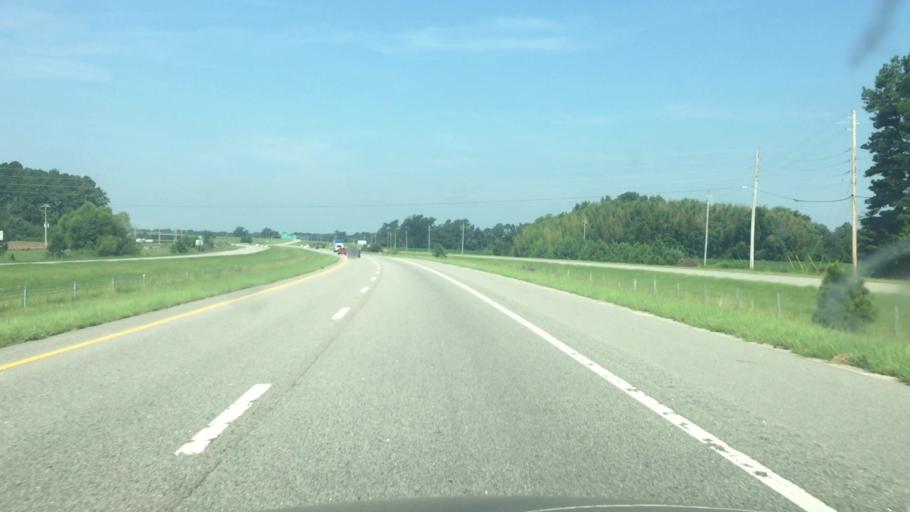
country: US
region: North Carolina
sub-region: Robeson County
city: Lumberton
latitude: 34.5929
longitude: -79.0753
